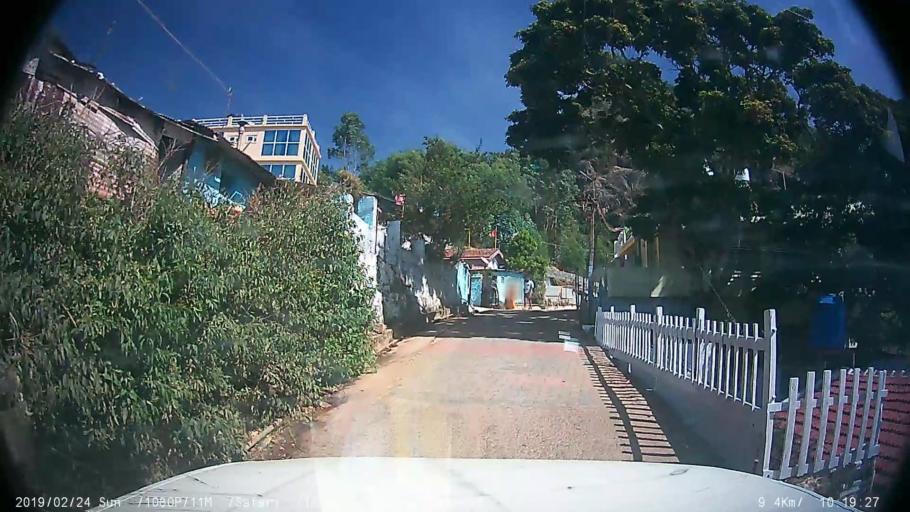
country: IN
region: Tamil Nadu
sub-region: Nilgiri
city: Ooty
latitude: 11.3867
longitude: 76.7198
